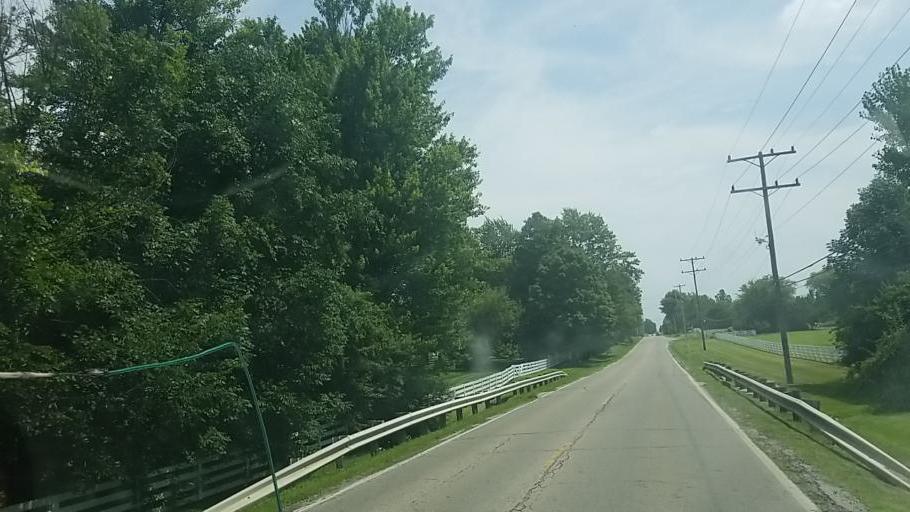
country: US
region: Ohio
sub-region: Franklin County
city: New Albany
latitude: 40.0540
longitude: -82.8328
